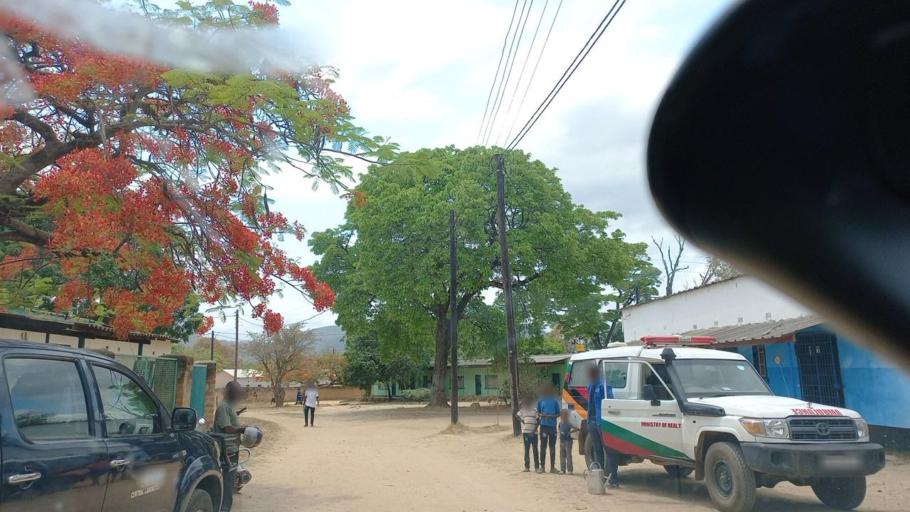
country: ZM
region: Lusaka
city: Luangwa
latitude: -15.1088
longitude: 29.7247
